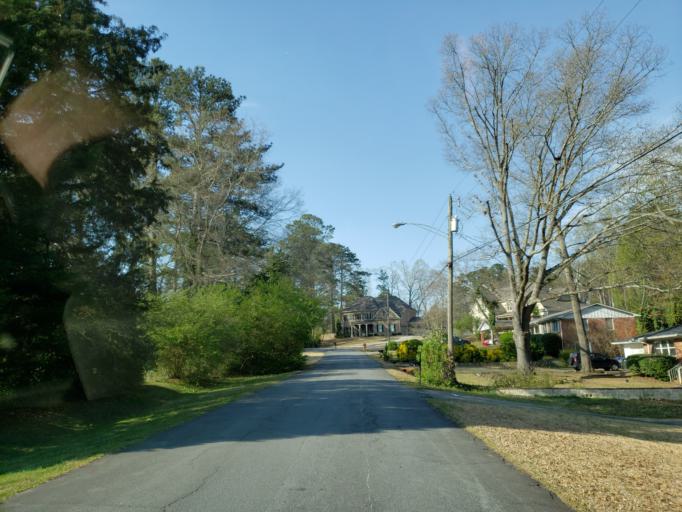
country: US
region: Georgia
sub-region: Cobb County
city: Marietta
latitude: 33.9796
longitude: -84.4651
